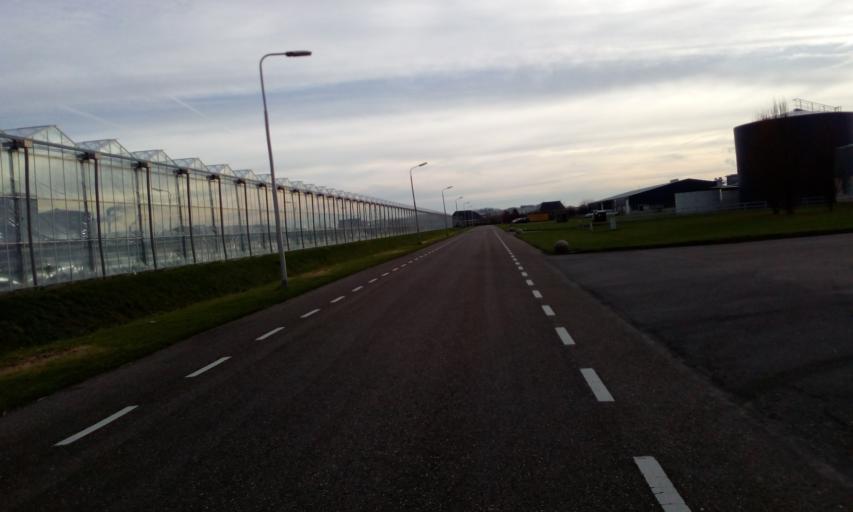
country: NL
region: South Holland
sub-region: Gemeente Lansingerland
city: Bleiswijk
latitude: 51.9882
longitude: 4.5269
